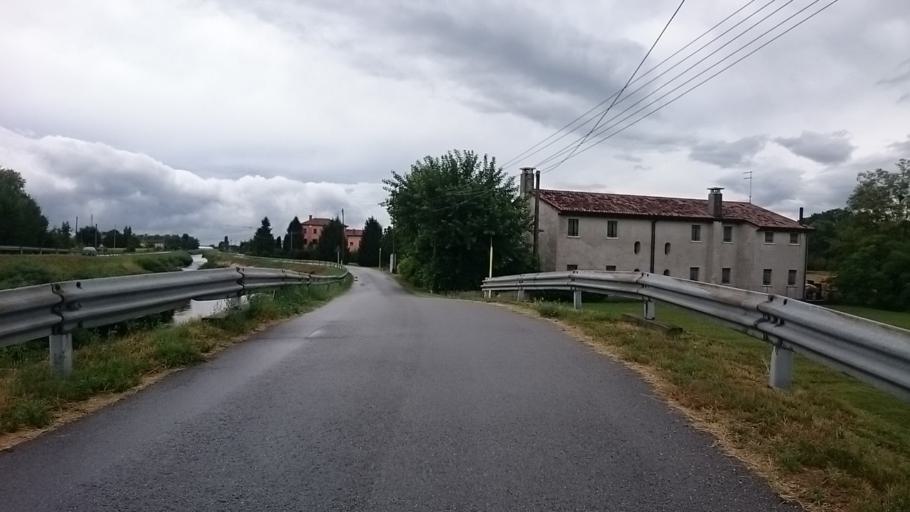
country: IT
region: Veneto
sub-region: Provincia di Treviso
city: Sant'Andrea
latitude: 45.6462
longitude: 11.9219
